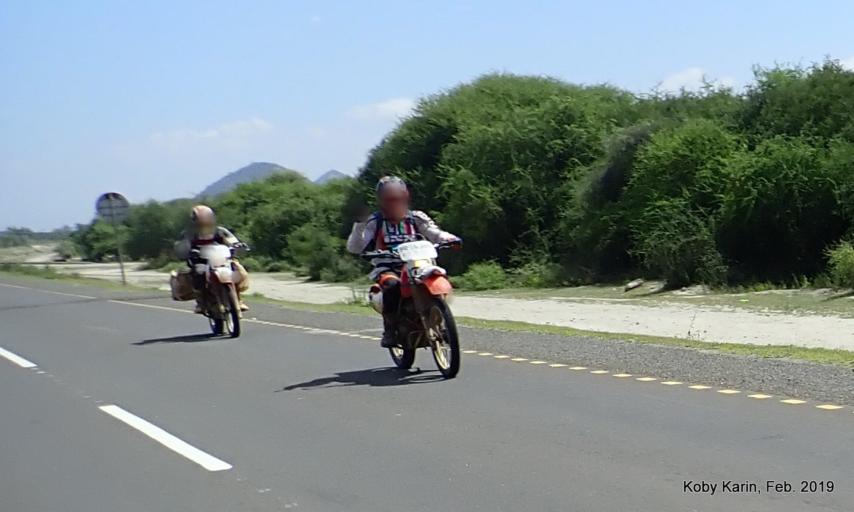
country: TZ
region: Manyara
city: Magugu
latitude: -3.8646
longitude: 35.8284
